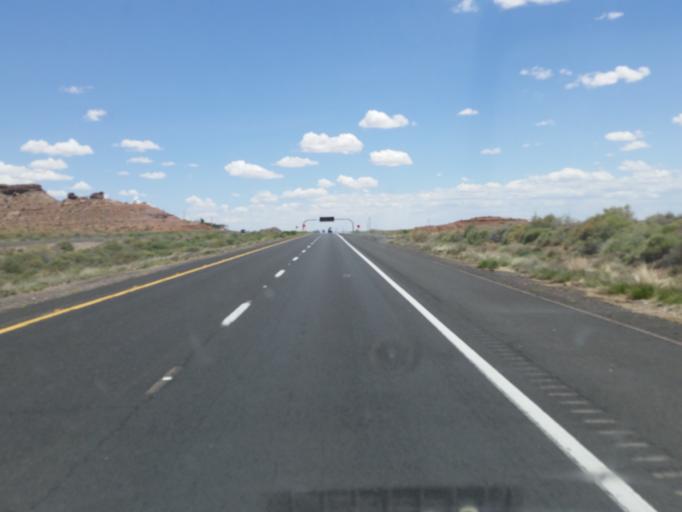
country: US
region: Arizona
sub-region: Navajo County
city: Joseph City
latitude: 34.9220
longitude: -110.2594
